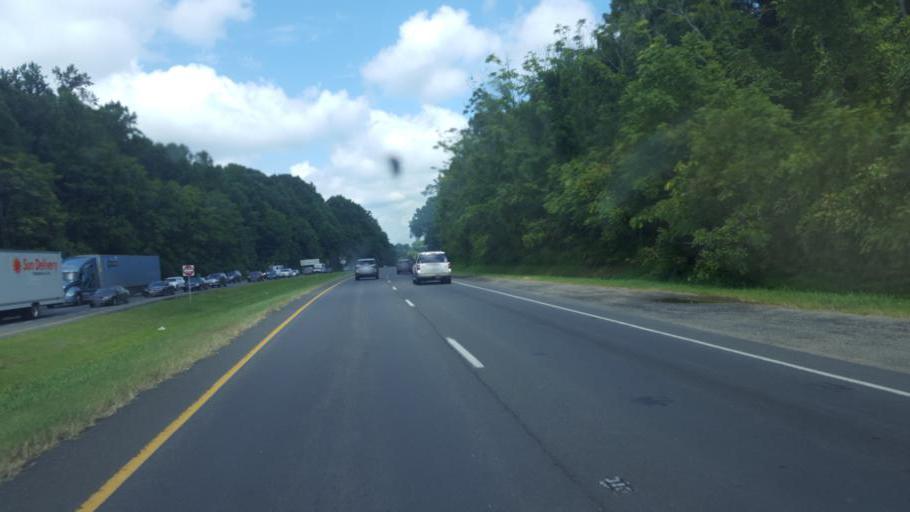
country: US
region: Virginia
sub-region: Fauquier County
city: Warrenton
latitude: 38.6874
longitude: -77.7868
